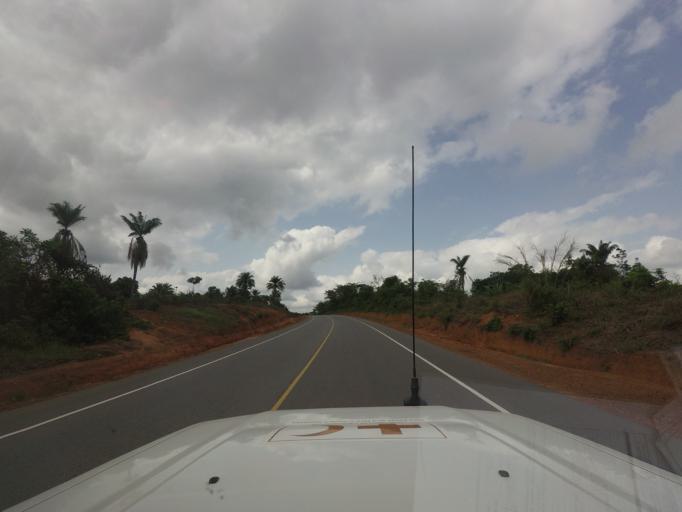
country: LR
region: Nimba
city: Sanniquellie
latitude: 7.1768
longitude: -9.0329
